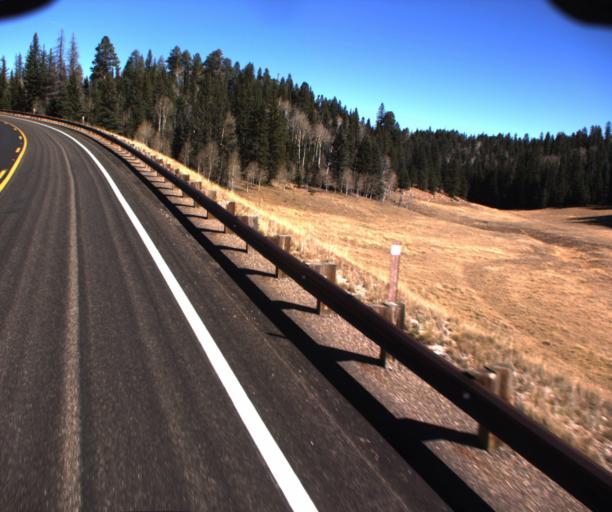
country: US
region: Arizona
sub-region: Coconino County
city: Grand Canyon
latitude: 36.4454
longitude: -112.1305
